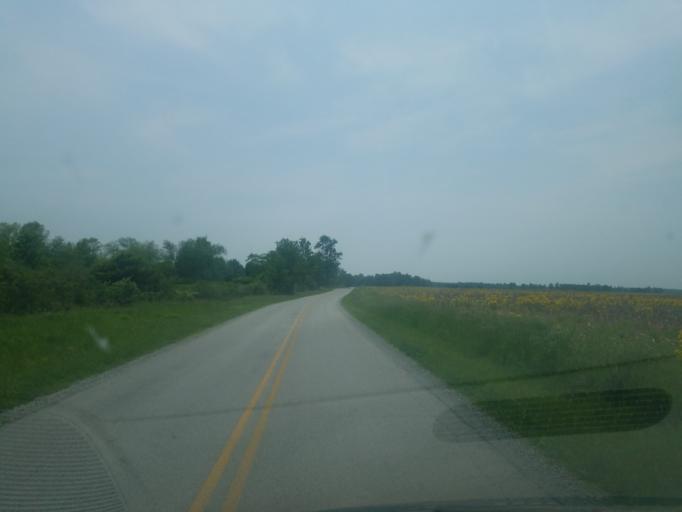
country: US
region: Ohio
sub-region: Wyandot County
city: Upper Sandusky
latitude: 40.7354
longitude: -83.2940
